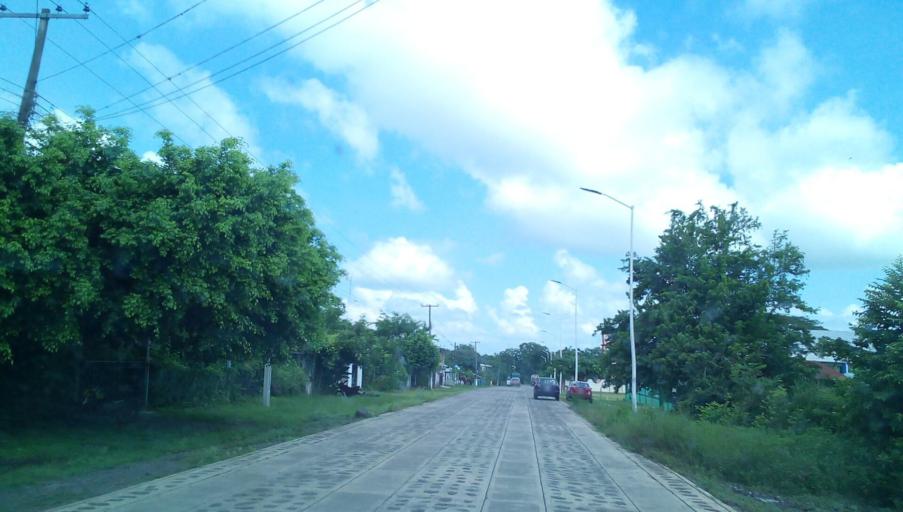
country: MX
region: Veracruz
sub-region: Citlaltepetl
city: Las Sabinas
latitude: 21.3611
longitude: -97.9008
